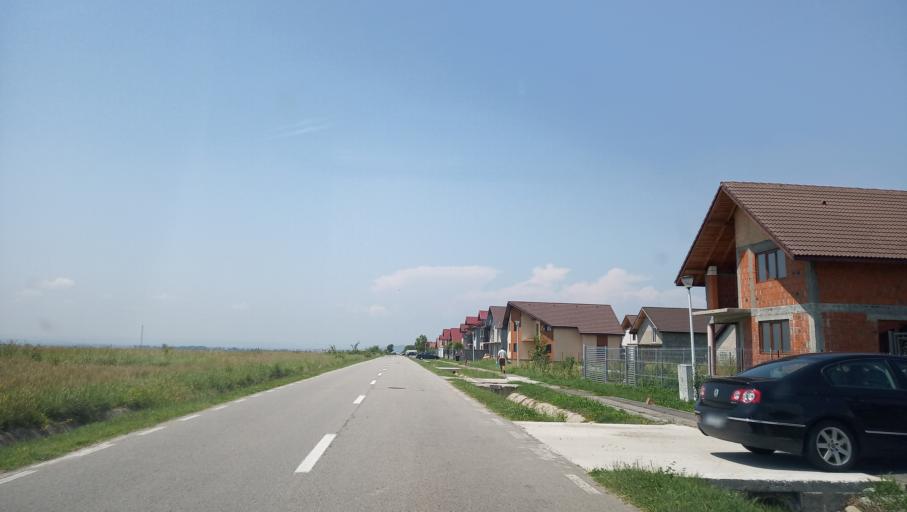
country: RO
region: Gorj
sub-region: Comuna Turcinesti
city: Turcinesti
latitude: 45.0661
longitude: 23.3365
